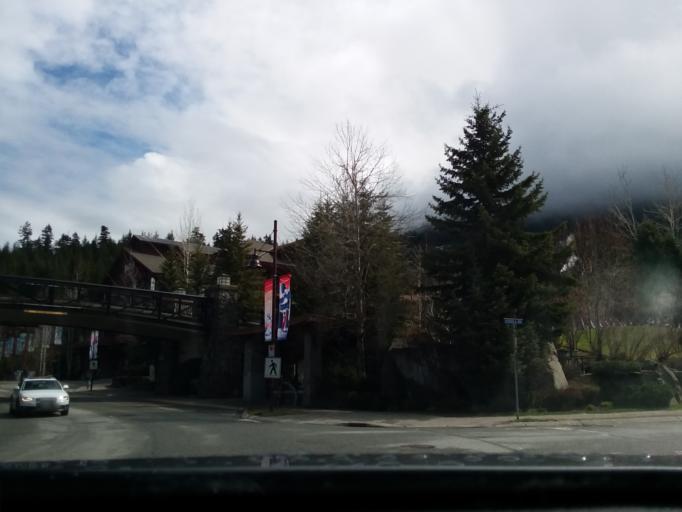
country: CA
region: British Columbia
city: Whistler
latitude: 50.0942
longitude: -122.9905
